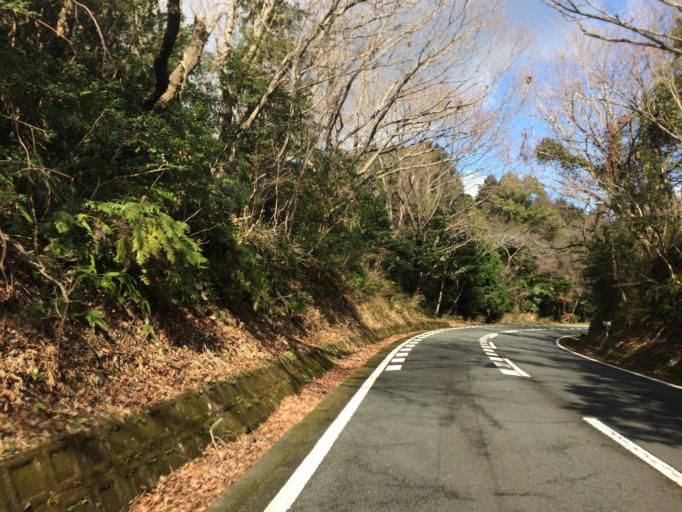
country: JP
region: Shizuoka
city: Shizuoka-shi
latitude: 34.9729
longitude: 138.4483
